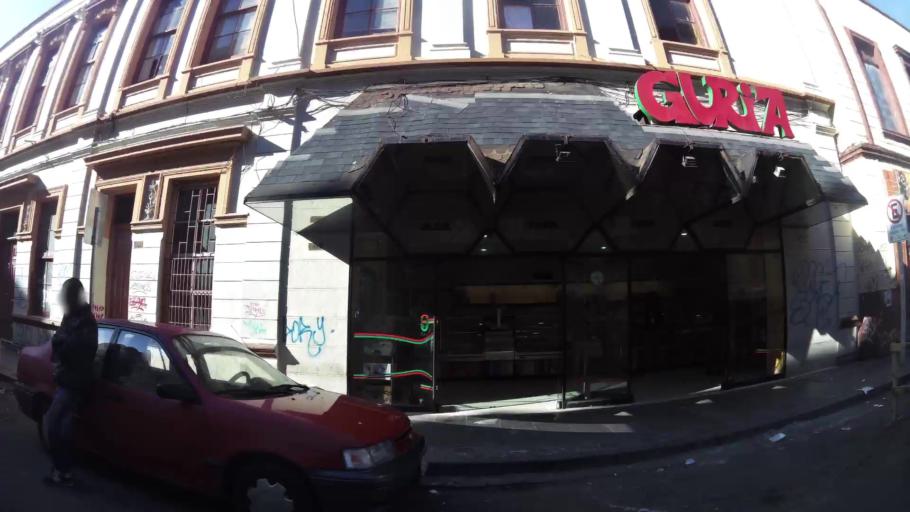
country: CL
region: Valparaiso
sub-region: Provincia de Valparaiso
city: Valparaiso
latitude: -33.0446
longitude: -71.6228
